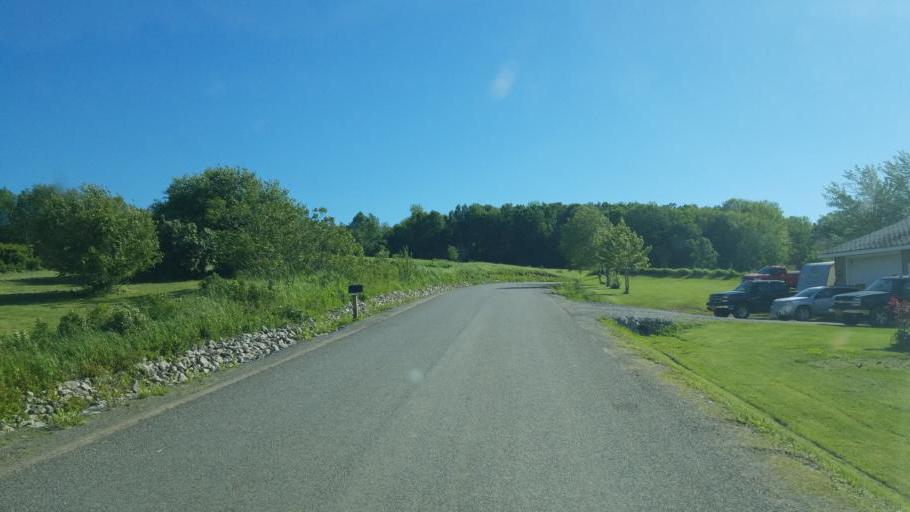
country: US
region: New York
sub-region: Montgomery County
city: Saint Johnsville
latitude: 42.9782
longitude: -74.7780
